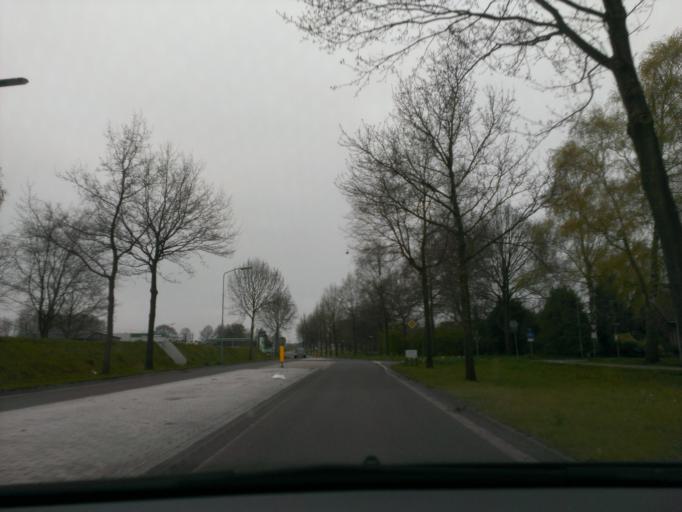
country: NL
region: Gelderland
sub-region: Gemeente Epe
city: Vaassen
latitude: 52.2854
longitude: 5.9733
